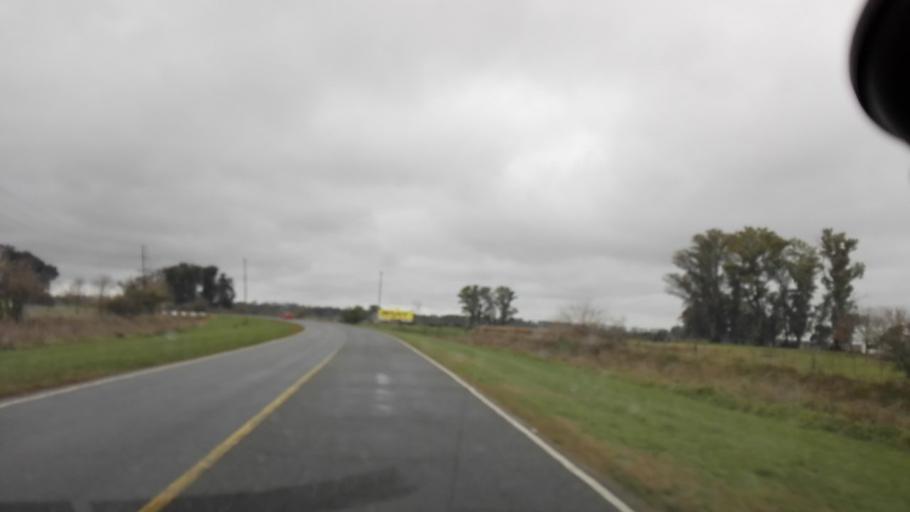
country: AR
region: Buenos Aires
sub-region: Partido de Brandsen
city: Brandsen
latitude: -35.1812
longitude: -58.2665
